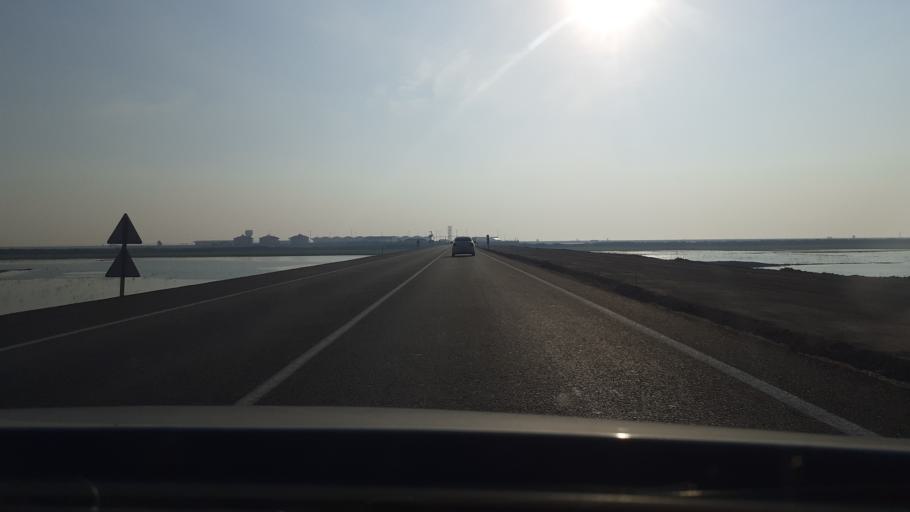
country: TR
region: Hatay
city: Serinyol
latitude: 36.3665
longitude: 36.2665
